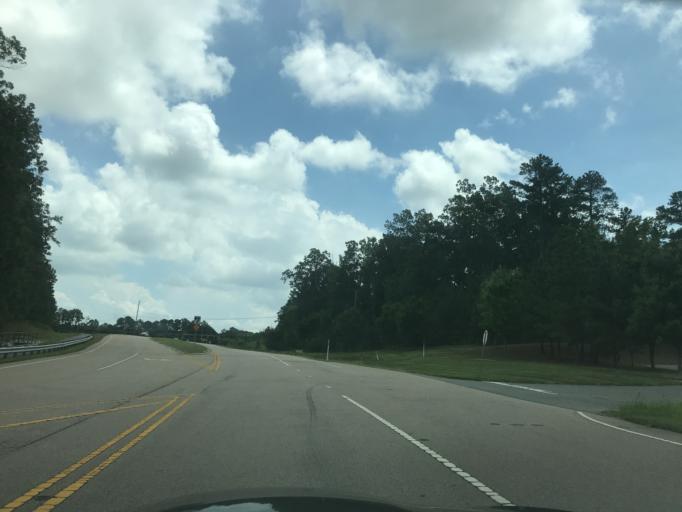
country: US
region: North Carolina
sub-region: Wake County
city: Morrisville
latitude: 35.8781
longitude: -78.8846
